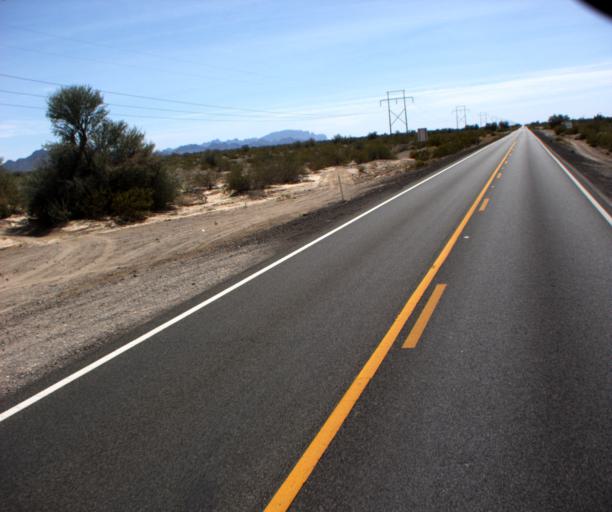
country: US
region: Arizona
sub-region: La Paz County
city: Quartzsite
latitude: 33.6494
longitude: -114.2171
